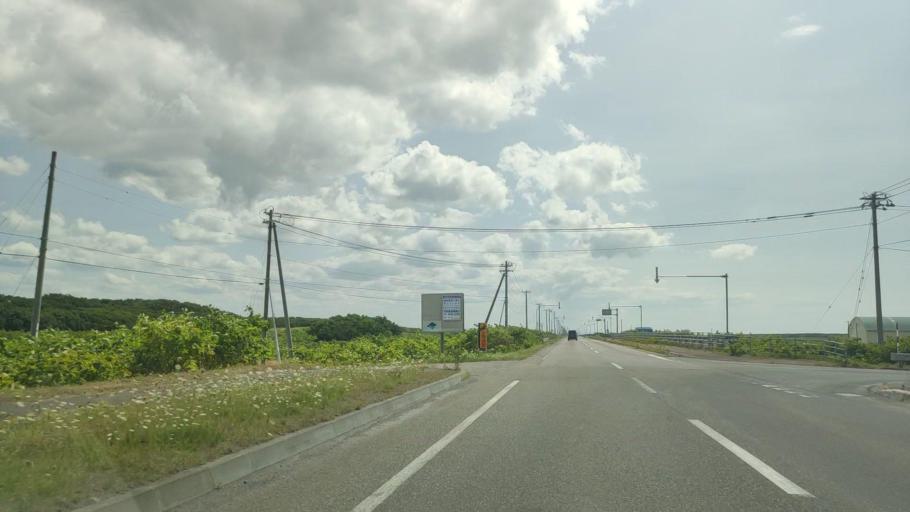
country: JP
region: Hokkaido
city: Makubetsu
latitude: 44.8678
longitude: 141.7529
